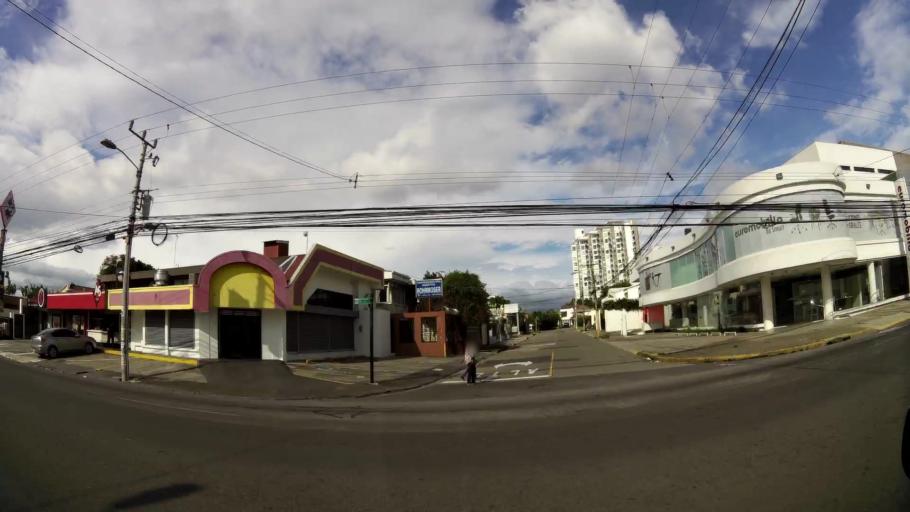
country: CR
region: San Jose
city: San Rafael
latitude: 9.9376
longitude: -84.1141
